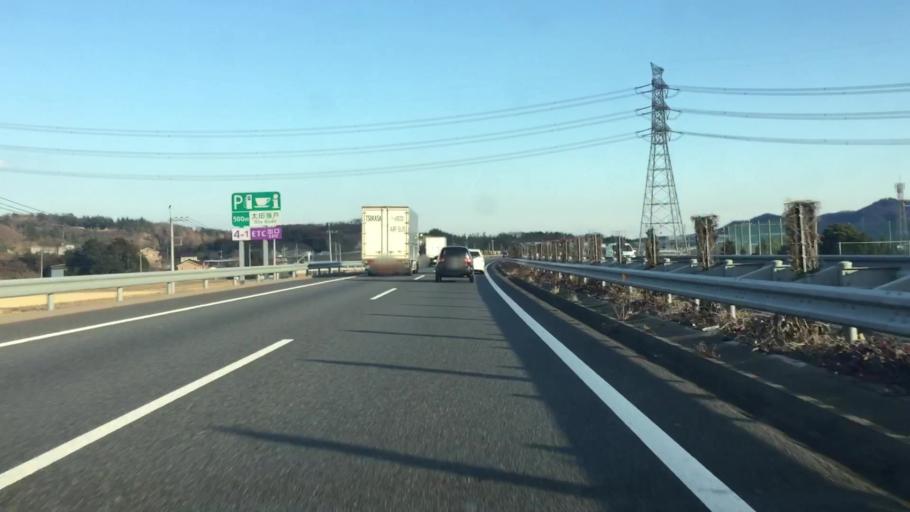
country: JP
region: Gunma
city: Ota
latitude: 36.3431
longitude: 139.3385
